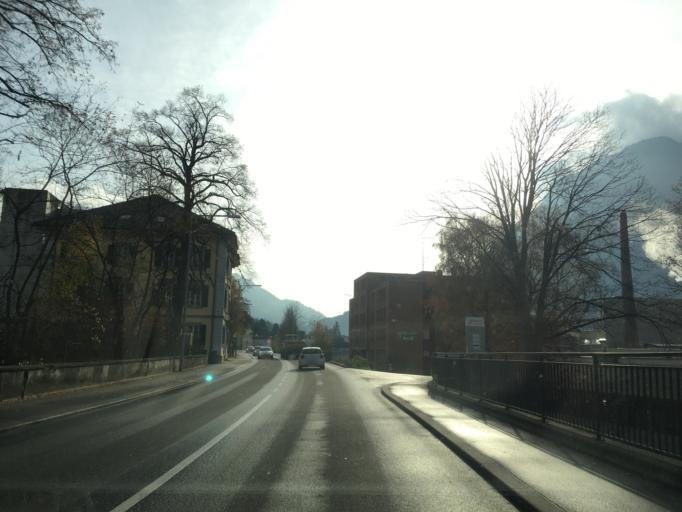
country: AT
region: Vorarlberg
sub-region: Politischer Bezirk Bludenz
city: Bludenz
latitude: 47.1527
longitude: 9.8230
